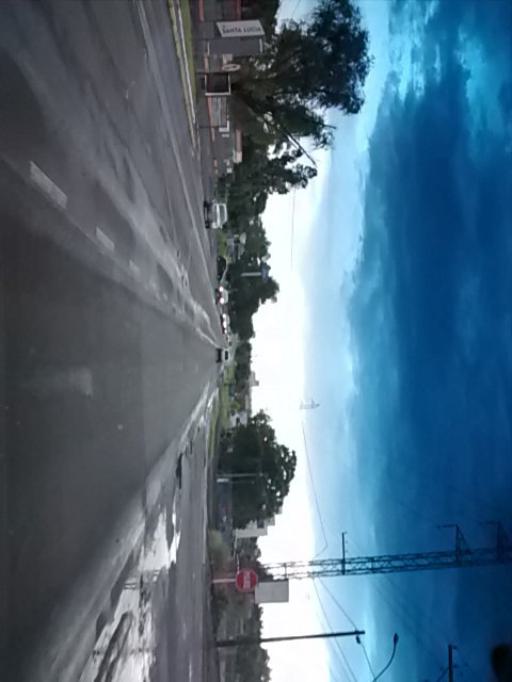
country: BR
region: Rio Grande do Sul
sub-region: Santa Maria
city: Santa Maria
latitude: -29.7224
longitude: -53.8069
